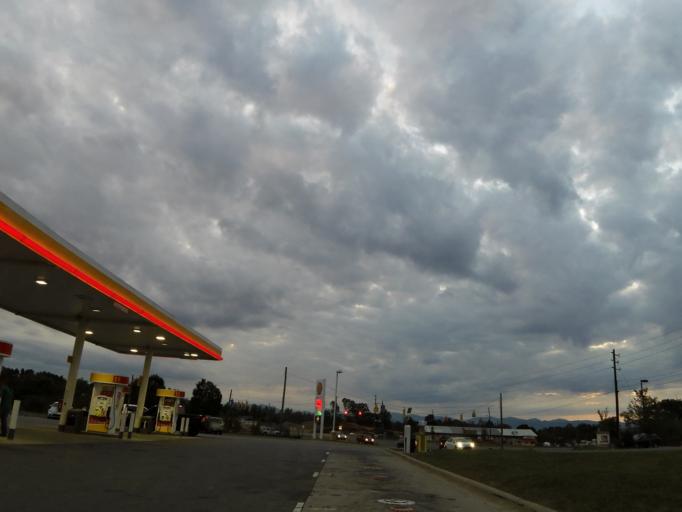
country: US
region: North Carolina
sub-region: Buncombe County
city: Weaverville
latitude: 35.7087
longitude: -82.5777
